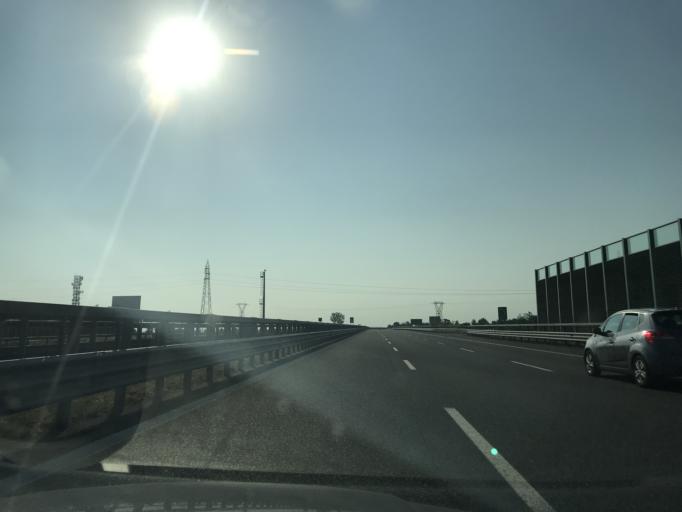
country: IT
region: Lombardy
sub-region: Provincia di Bergamo
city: Casirate d'Adda
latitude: 45.5068
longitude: 9.5617
